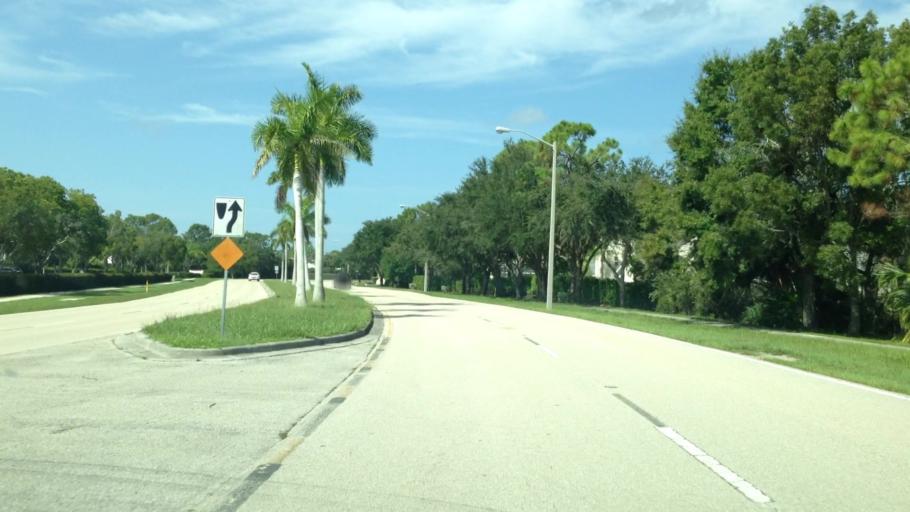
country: US
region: Florida
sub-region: Lee County
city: Bonita Springs
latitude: 26.3178
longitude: -81.8078
